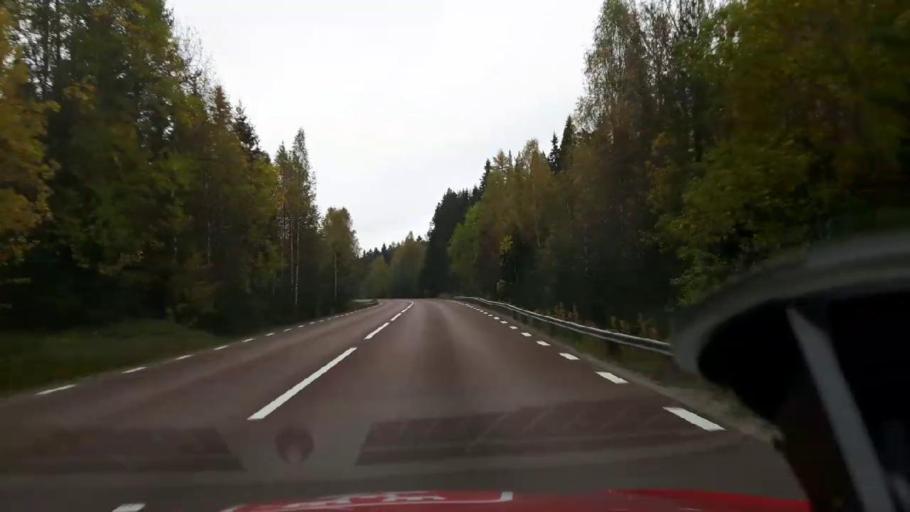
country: SE
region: Jaemtland
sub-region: Harjedalens Kommun
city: Sveg
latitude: 62.3374
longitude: 14.7290
